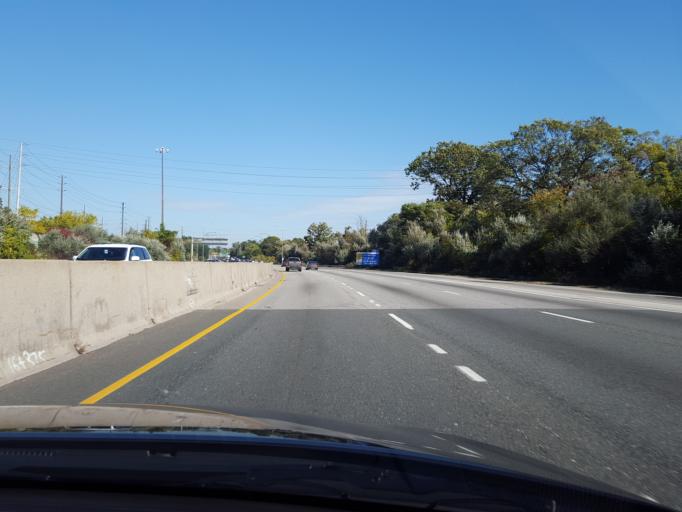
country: CA
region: Ontario
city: Mississauga
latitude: 43.5530
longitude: -79.6128
